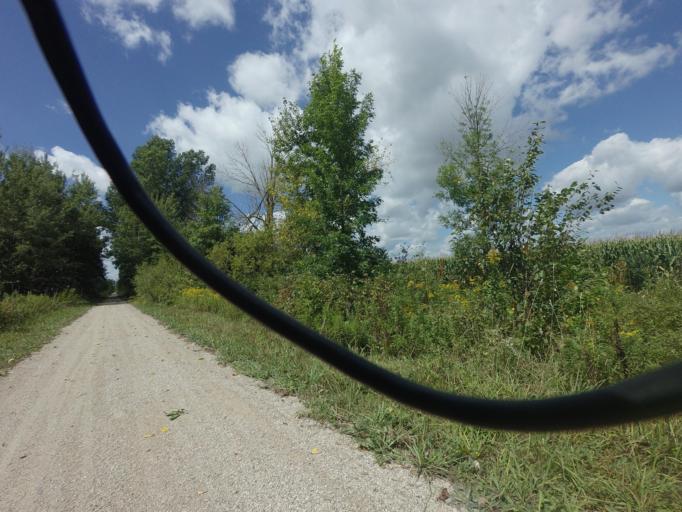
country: CA
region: Ontario
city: North Perth
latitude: 43.5664
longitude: -80.9496
